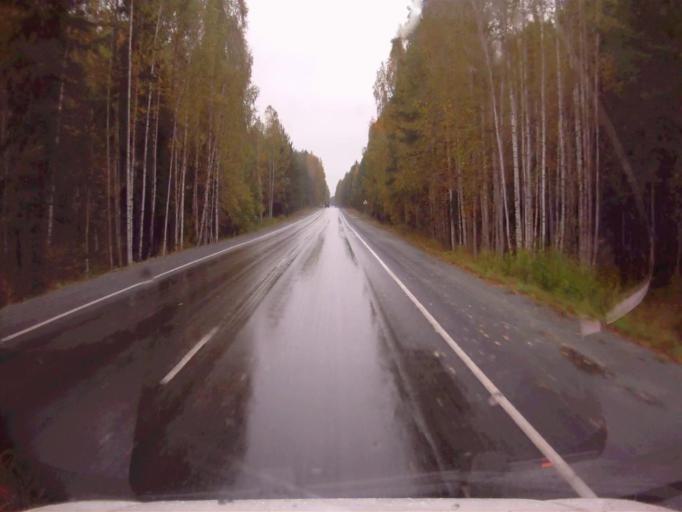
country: RU
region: Chelyabinsk
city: Tayginka
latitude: 55.5815
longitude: 60.6398
